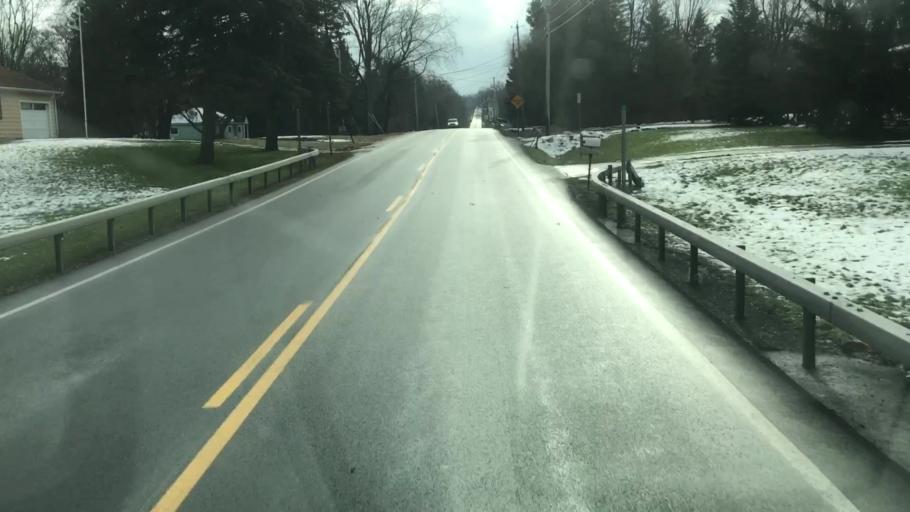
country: US
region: New York
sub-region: Onondaga County
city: Skaneateles
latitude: 42.8635
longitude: -76.4018
